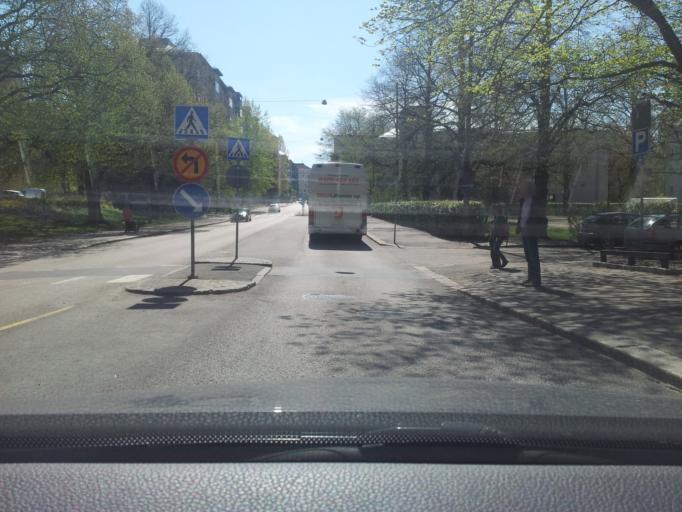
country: FI
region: Uusimaa
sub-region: Helsinki
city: Helsinki
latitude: 60.1873
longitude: 24.9145
